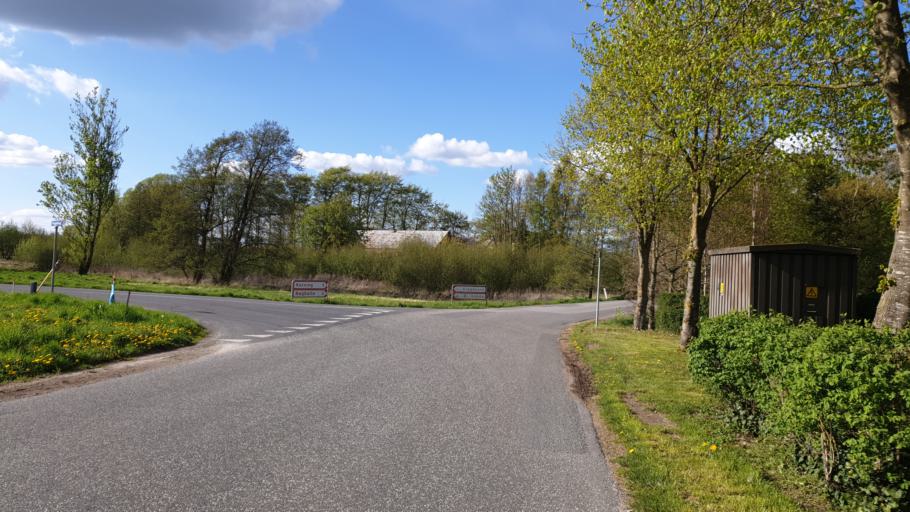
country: DK
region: Central Jutland
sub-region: Hedensted Kommune
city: Hedensted
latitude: 55.8136
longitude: 9.6580
